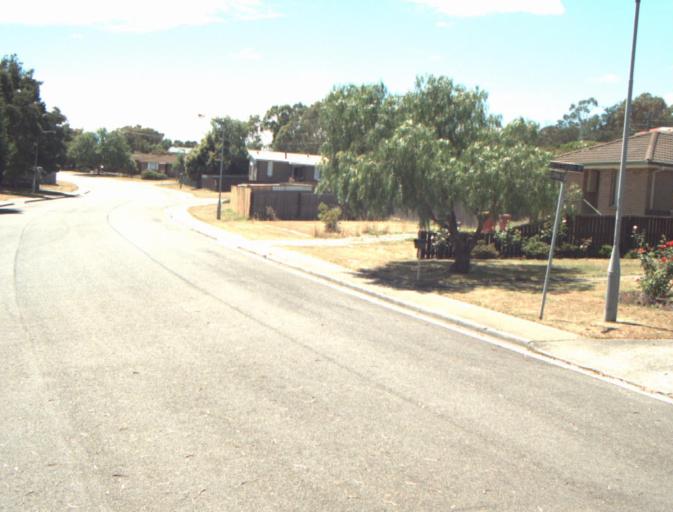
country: AU
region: Tasmania
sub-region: Launceston
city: Mayfield
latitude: -41.3806
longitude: 147.1346
